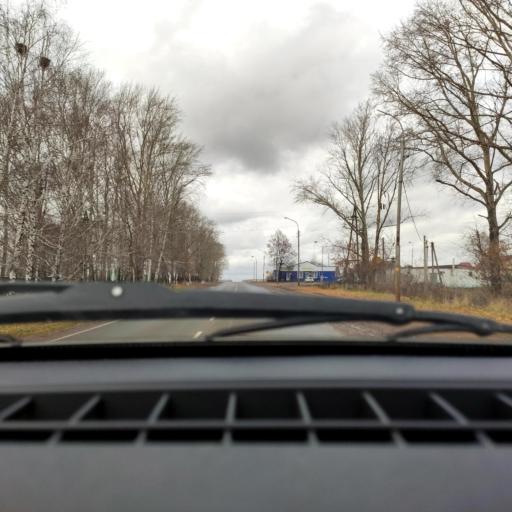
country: RU
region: Bashkortostan
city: Asanovo
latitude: 54.9594
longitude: 55.5511
